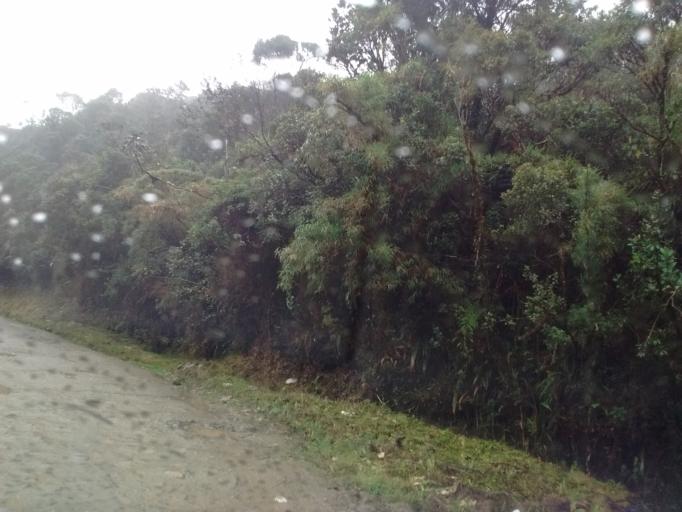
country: CO
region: Cauca
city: Paispamba
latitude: 2.1679
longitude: -76.4200
